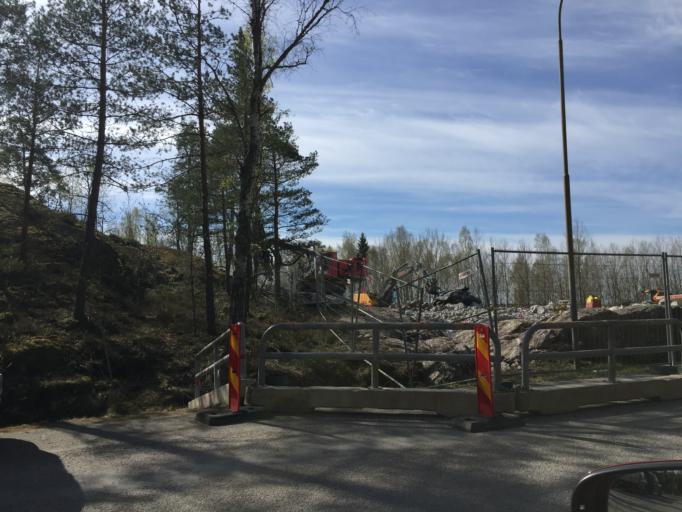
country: SE
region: Stockholm
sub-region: Salems Kommun
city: Ronninge
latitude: 59.2065
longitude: 17.7751
